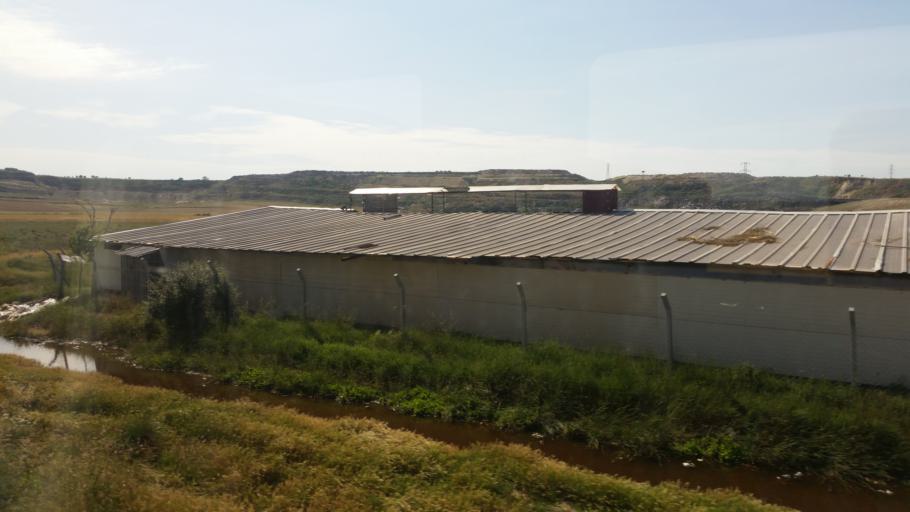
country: TR
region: Tekirdag
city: Corlu
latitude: 41.1866
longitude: 27.8002
